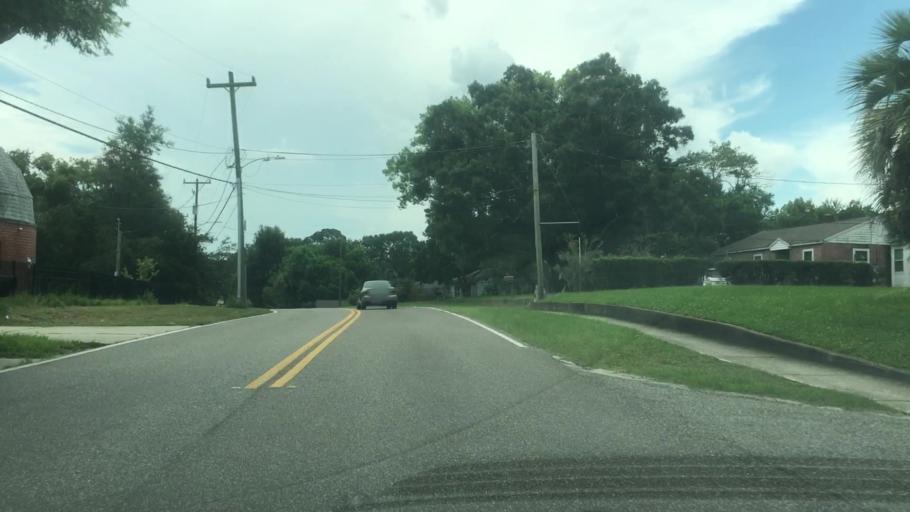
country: US
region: Florida
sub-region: Duval County
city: Jacksonville
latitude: 30.3161
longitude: -81.5473
